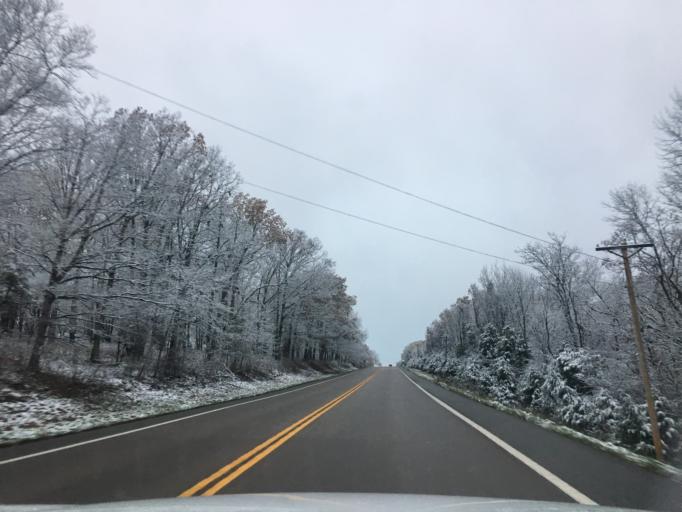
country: US
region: Missouri
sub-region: Osage County
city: Linn
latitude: 38.4704
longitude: -91.7785
